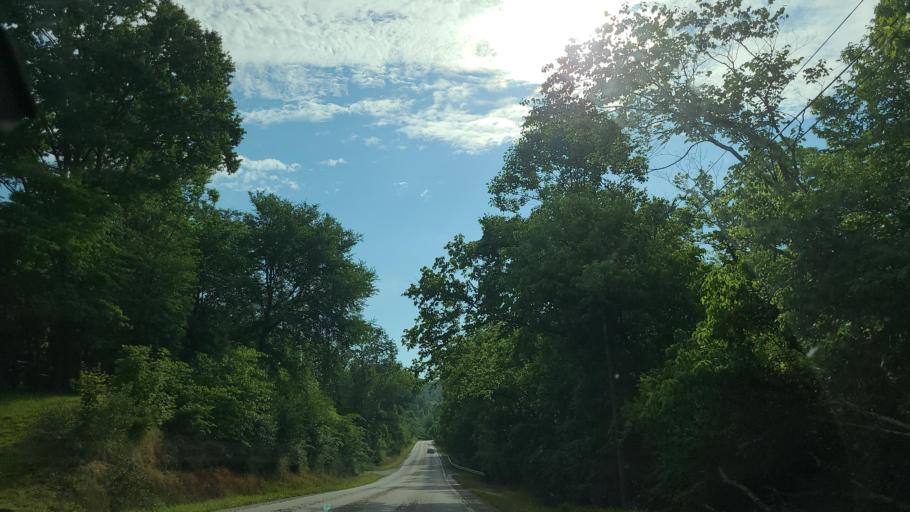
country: US
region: Kentucky
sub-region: Whitley County
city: Williamsburg
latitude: 36.7308
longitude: -84.1224
